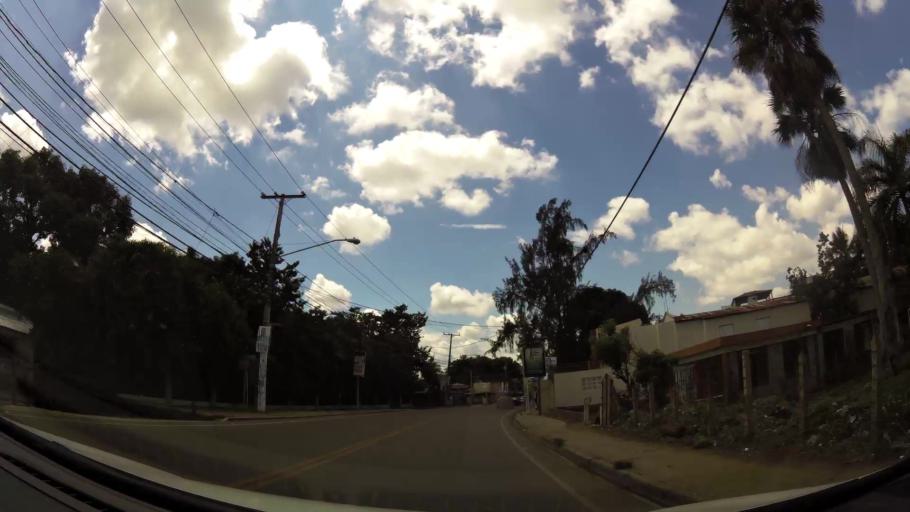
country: DO
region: Santiago
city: Santiago de los Caballeros
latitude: 19.4759
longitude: -70.6707
